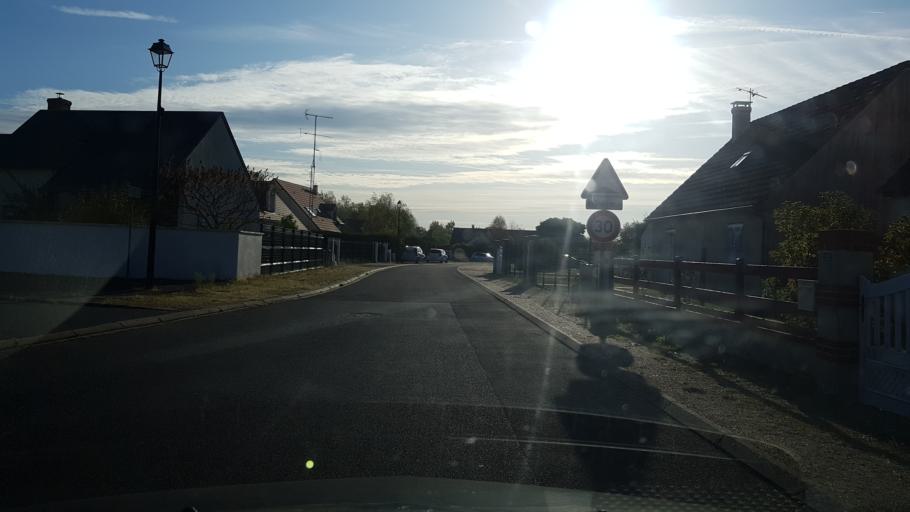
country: FR
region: Centre
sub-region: Departement du Loiret
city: Cerdon
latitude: 47.6883
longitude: 2.3372
